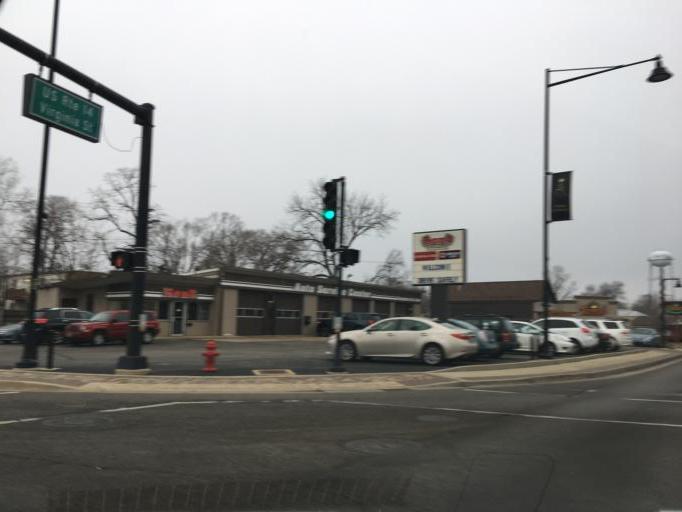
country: US
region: Illinois
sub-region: McHenry County
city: Crystal Lake
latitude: 42.2317
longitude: -88.3336
